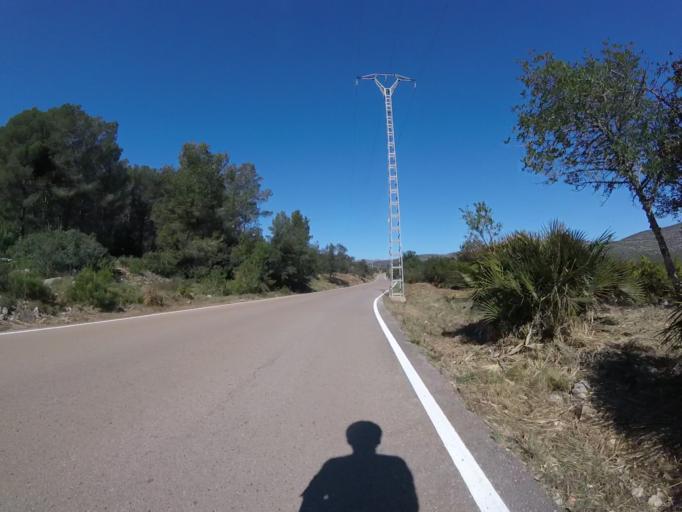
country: ES
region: Valencia
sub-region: Provincia de Castello
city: Santa Magdalena de Pulpis
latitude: 40.3649
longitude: 0.2779
